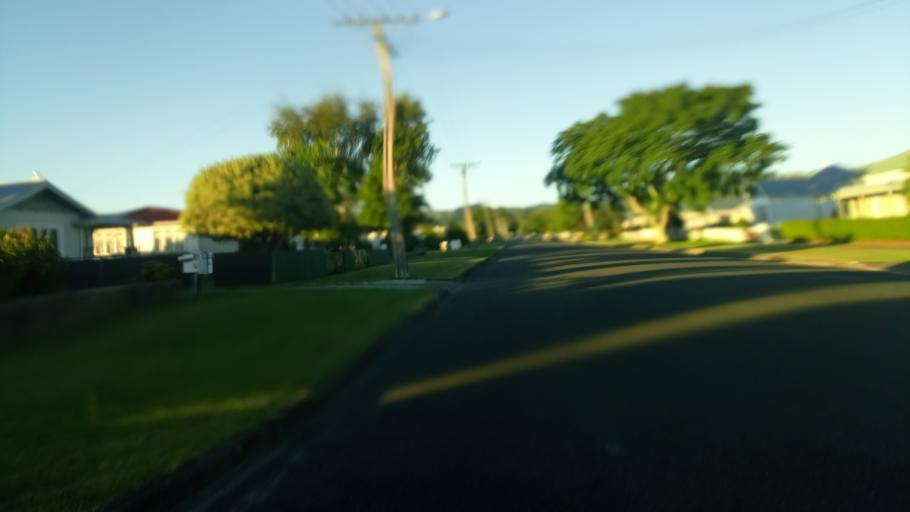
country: NZ
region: Gisborne
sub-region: Gisborne District
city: Gisborne
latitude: -38.6530
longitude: 178.0048
